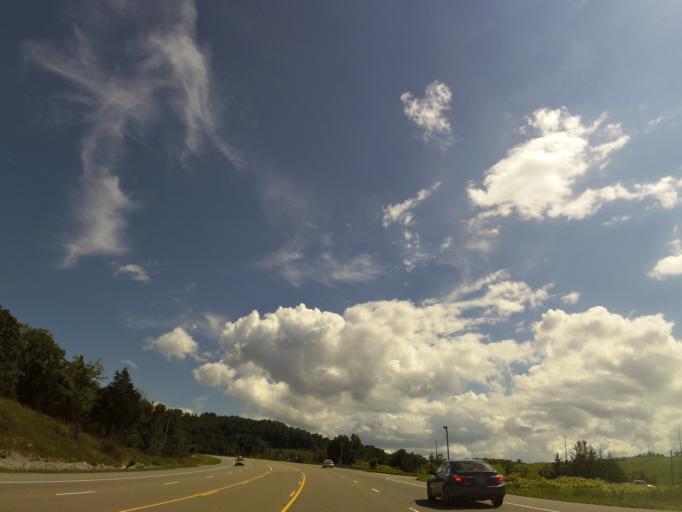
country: US
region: Tennessee
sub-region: Claiborne County
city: Tazewell
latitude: 36.4429
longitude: -83.5686
